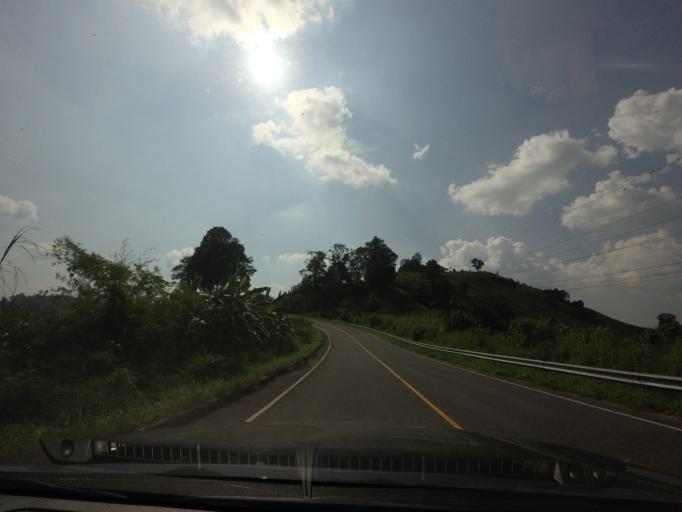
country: TH
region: Nan
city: Santi Suk
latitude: 18.9728
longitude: 100.9819
